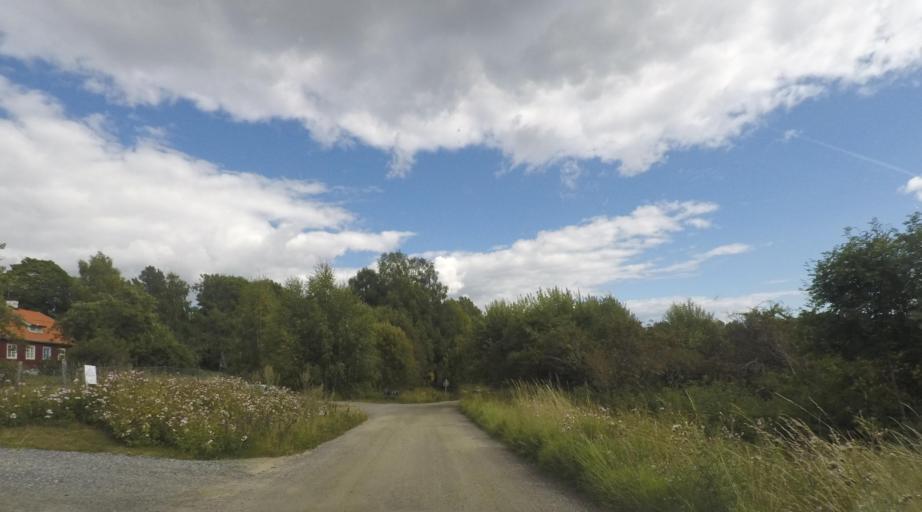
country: SE
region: Stockholm
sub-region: Sodertalje Kommun
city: Pershagen
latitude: 59.1203
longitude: 17.6544
